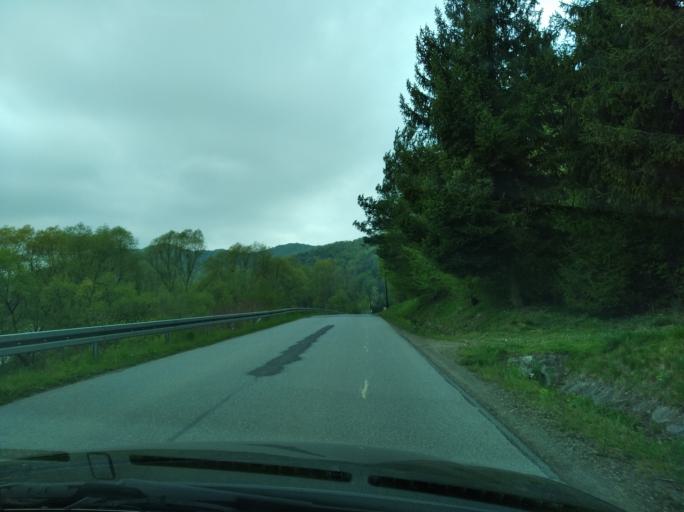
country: PL
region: Subcarpathian Voivodeship
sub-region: Powiat sanocki
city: Sanok
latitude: 49.6032
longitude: 22.2104
